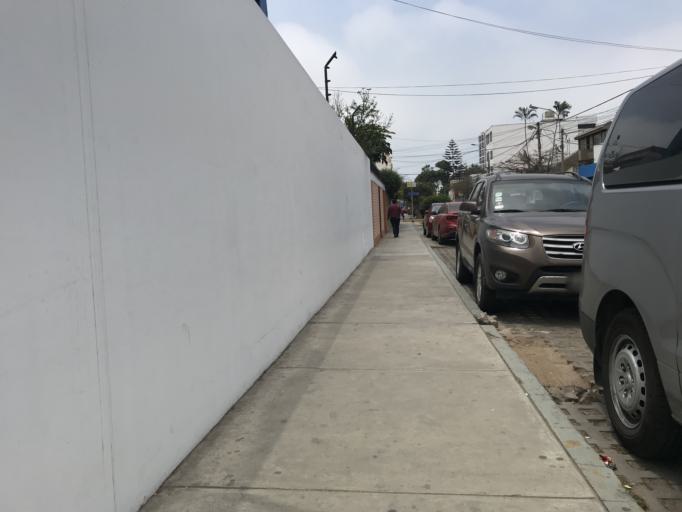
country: PE
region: Callao
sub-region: Callao
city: Callao
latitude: -12.0798
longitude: -77.0803
